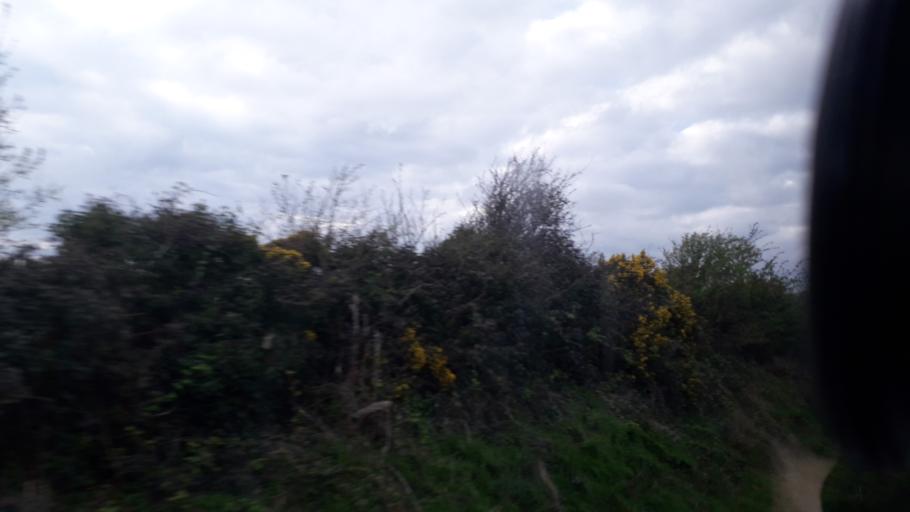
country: IE
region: Leinster
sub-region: An Iarmhi
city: An Muileann gCearr
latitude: 53.5849
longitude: -7.3811
